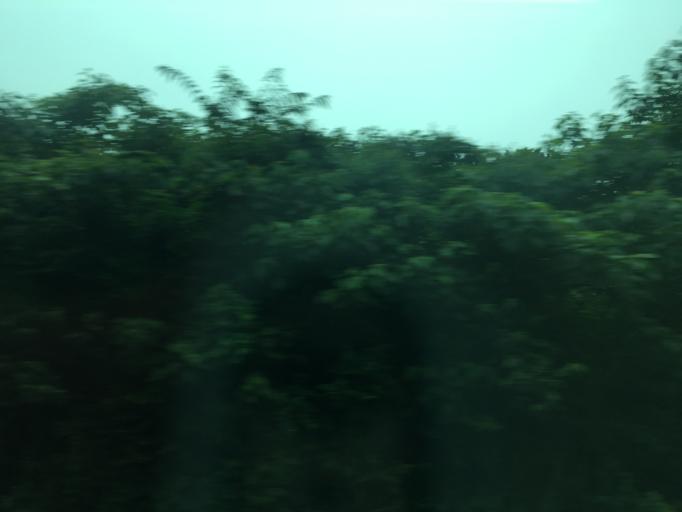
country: JP
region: Ibaraki
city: Koga
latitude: 36.1695
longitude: 139.7170
